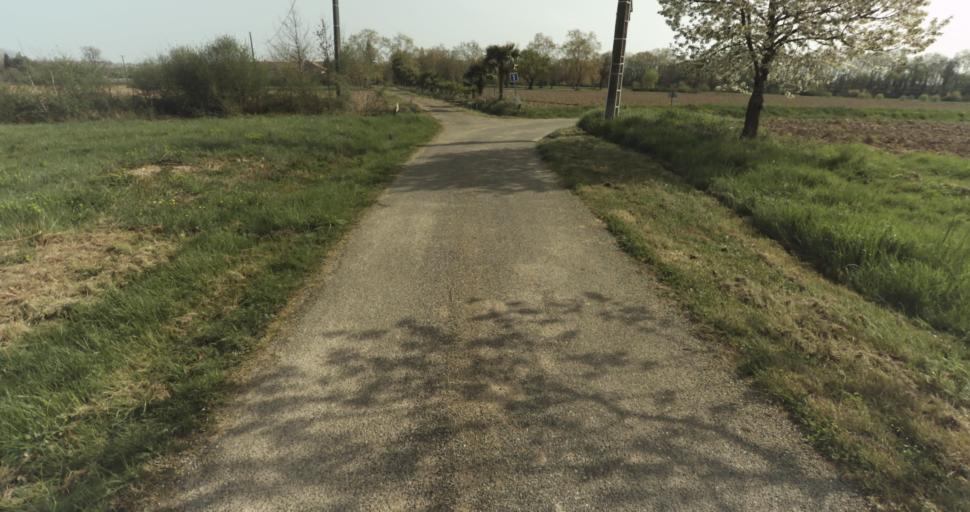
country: FR
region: Midi-Pyrenees
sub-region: Departement du Tarn-et-Garonne
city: Moissac
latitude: 44.0835
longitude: 1.0946
